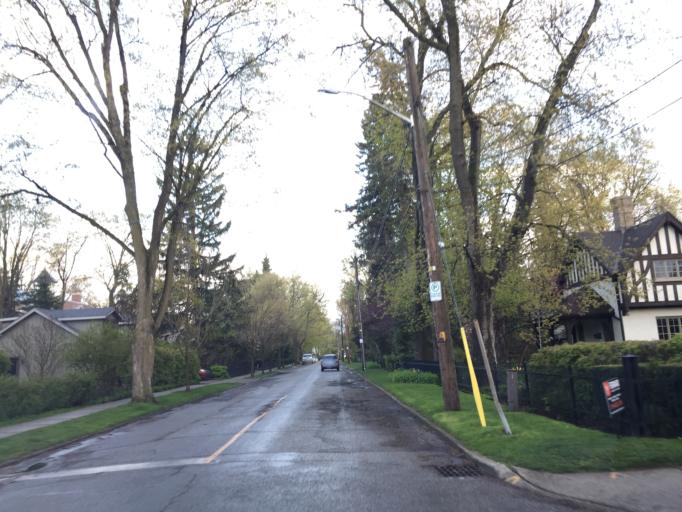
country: CA
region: Ontario
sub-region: Wellington County
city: Guelph
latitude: 43.5518
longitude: -80.2456
